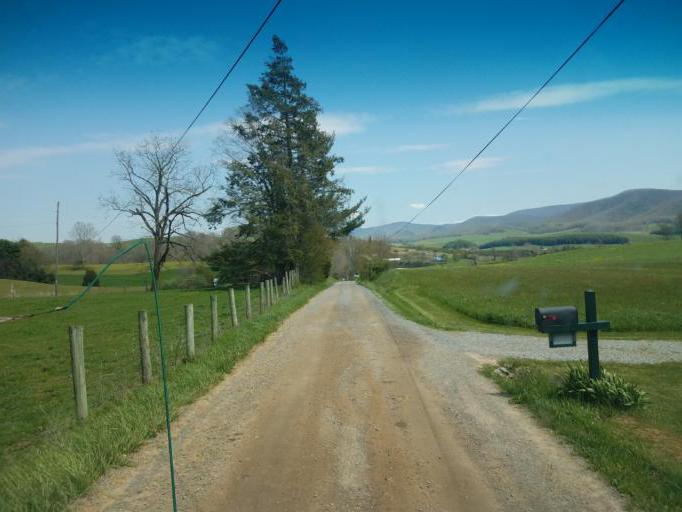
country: US
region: Virginia
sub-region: Smyth County
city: Marion
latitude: 36.7795
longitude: -81.4595
